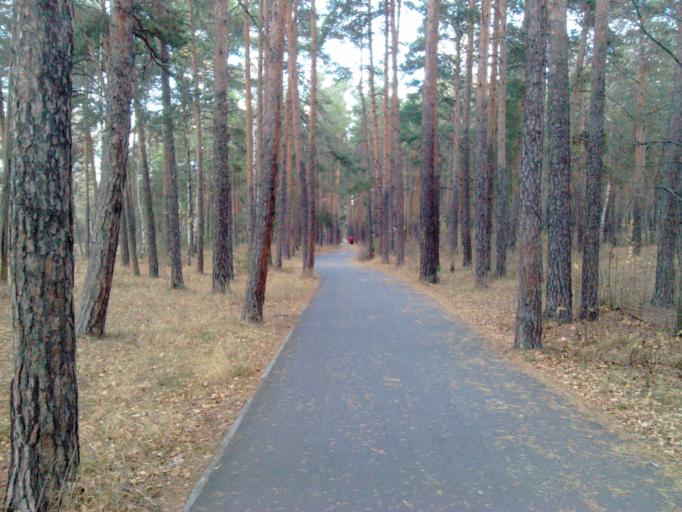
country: RU
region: Chelyabinsk
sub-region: Gorod Chelyabinsk
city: Chelyabinsk
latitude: 55.1646
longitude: 61.3592
